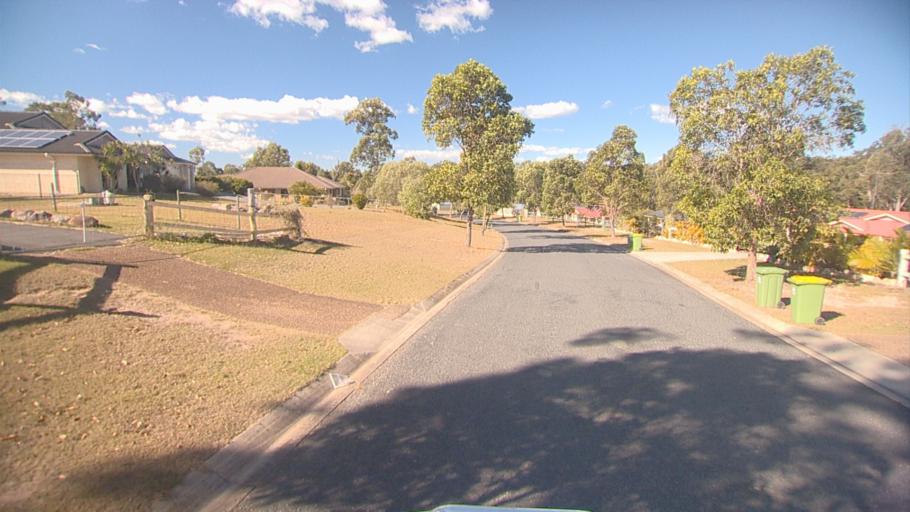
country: AU
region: Queensland
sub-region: Ipswich
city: Springfield Lakes
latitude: -27.7348
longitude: 152.9109
